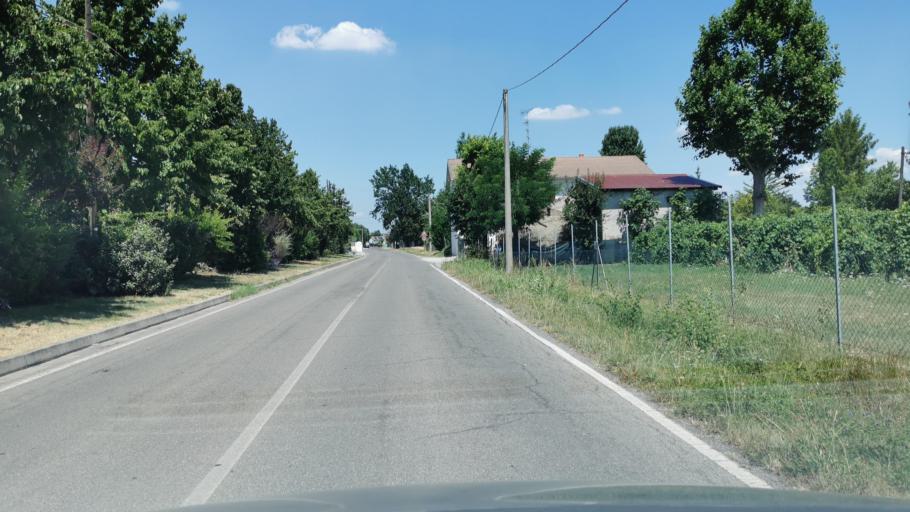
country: IT
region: Emilia-Romagna
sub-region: Provincia di Modena
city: Fossoli
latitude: 44.8164
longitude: 10.8952
